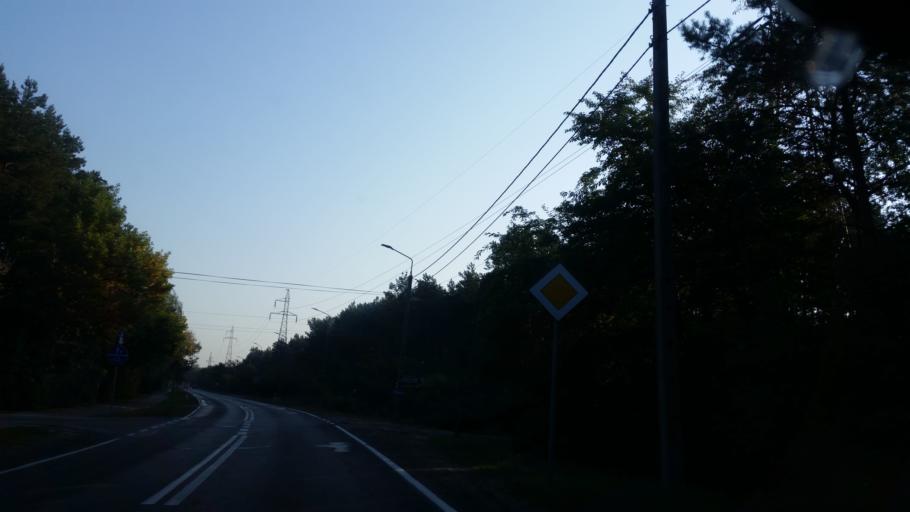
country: PL
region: Masovian Voivodeship
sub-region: Powiat otwocki
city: Jozefow
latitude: 52.1360
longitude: 21.2530
